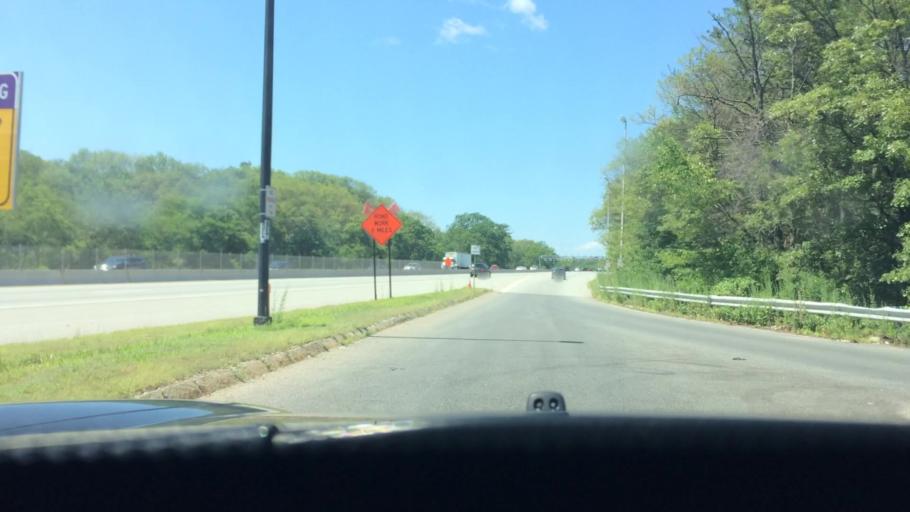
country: US
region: Massachusetts
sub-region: Middlesex County
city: Framingham Center
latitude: 42.3113
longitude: -71.4304
